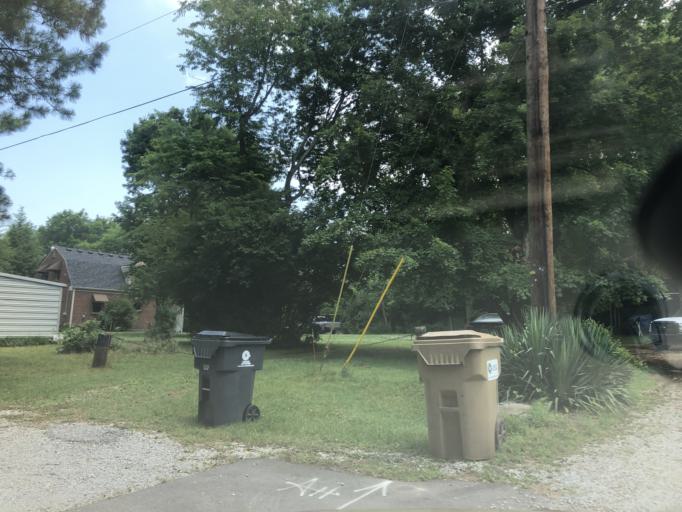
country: US
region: Tennessee
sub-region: Davidson County
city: Lakewood
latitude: 36.2130
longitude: -86.6285
